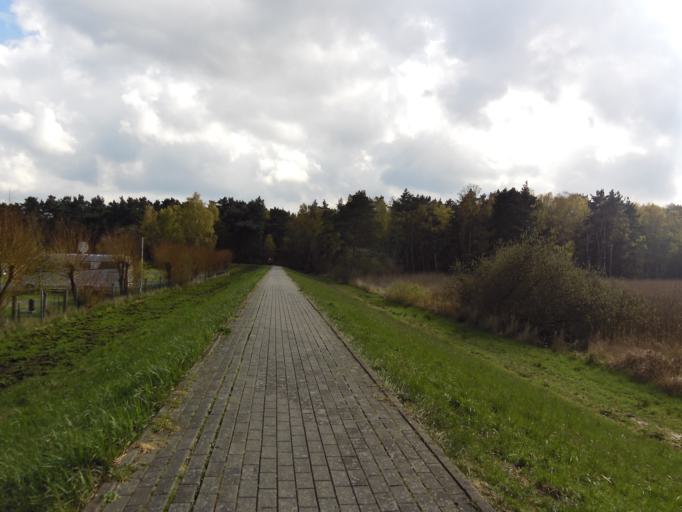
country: DE
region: Mecklenburg-Vorpommern
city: Zingst
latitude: 54.4393
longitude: 12.6598
